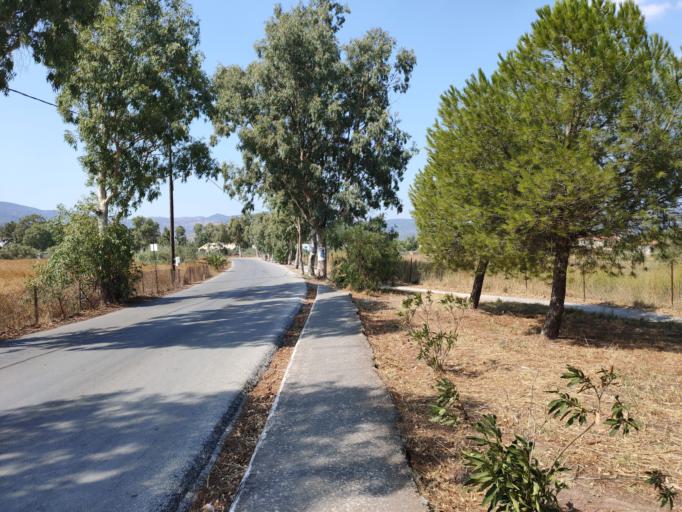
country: GR
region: North Aegean
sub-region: Nomos Lesvou
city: Kalloni
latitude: 39.2080
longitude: 26.2088
